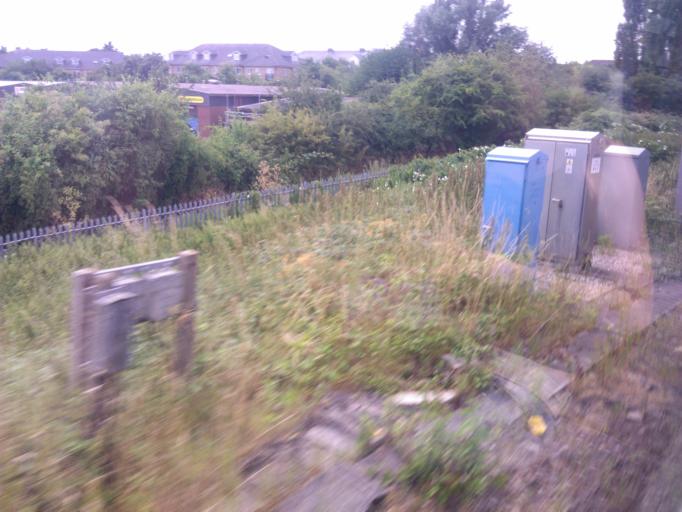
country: GB
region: England
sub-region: Essex
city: Colchester
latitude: 51.8998
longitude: 0.9007
